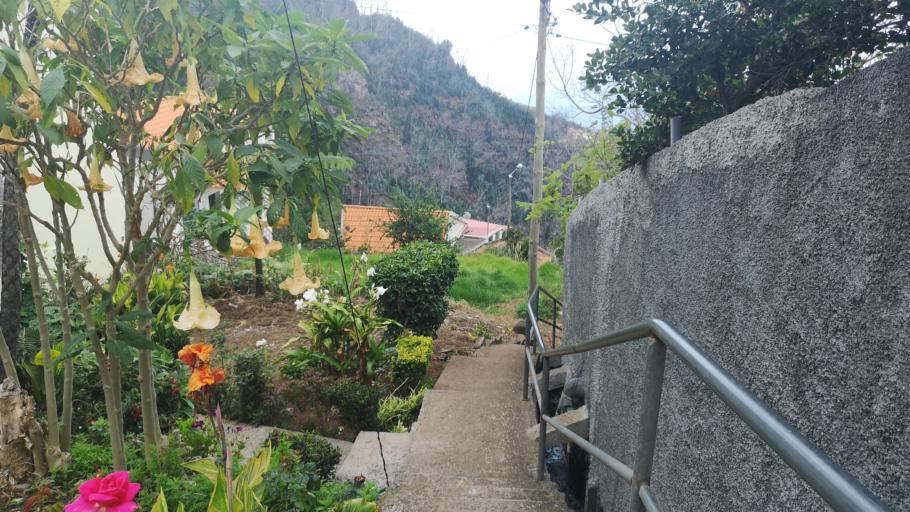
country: PT
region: Madeira
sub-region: Funchal
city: Nossa Senhora do Monte
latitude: 32.6753
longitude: -16.8910
